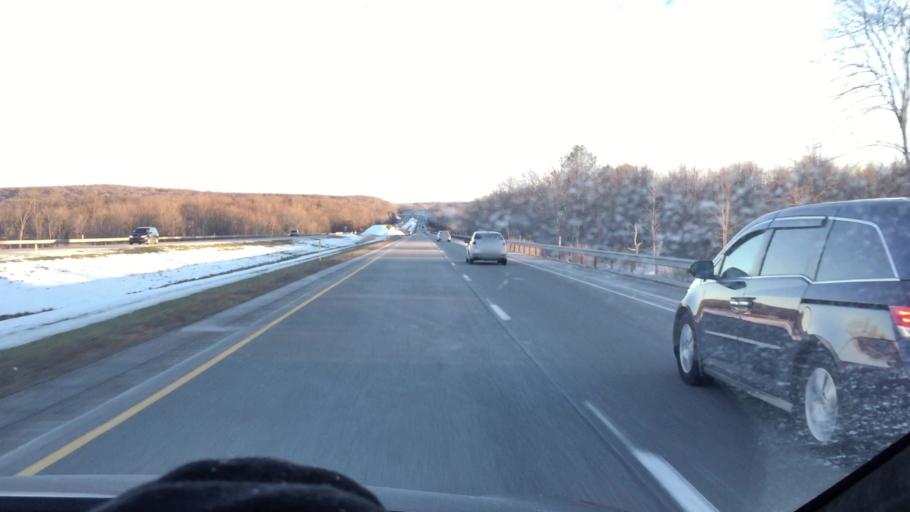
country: US
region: Pennsylvania
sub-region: Crawford County
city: Meadville
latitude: 41.6665
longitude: -80.2082
